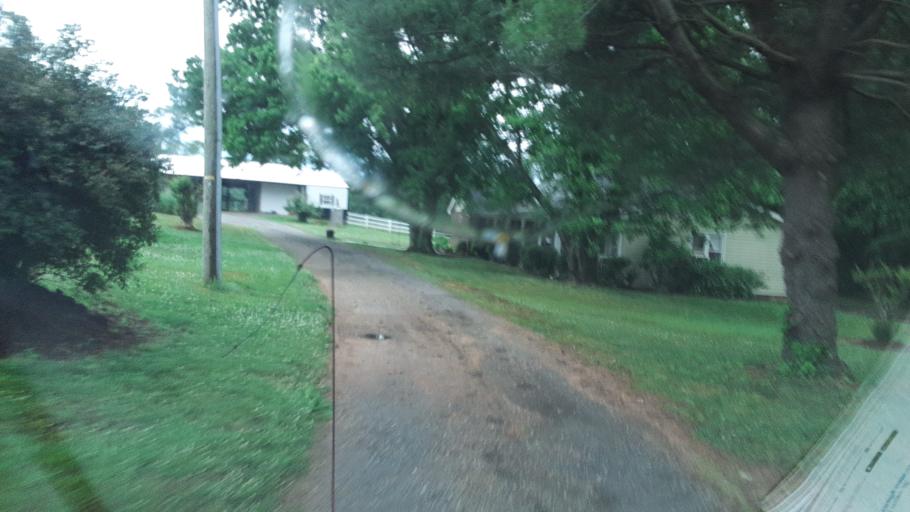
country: US
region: North Carolina
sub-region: Yadkin County
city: Yadkinville
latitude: 36.0512
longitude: -80.8254
